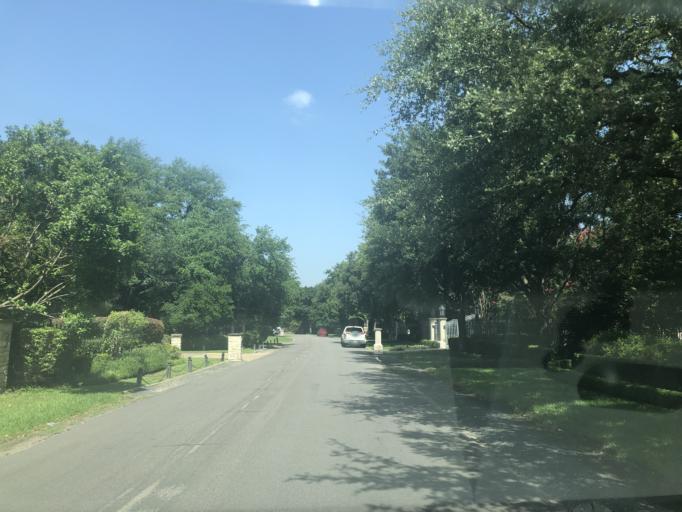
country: US
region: Texas
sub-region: Dallas County
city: University Park
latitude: 32.8693
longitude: -96.8230
